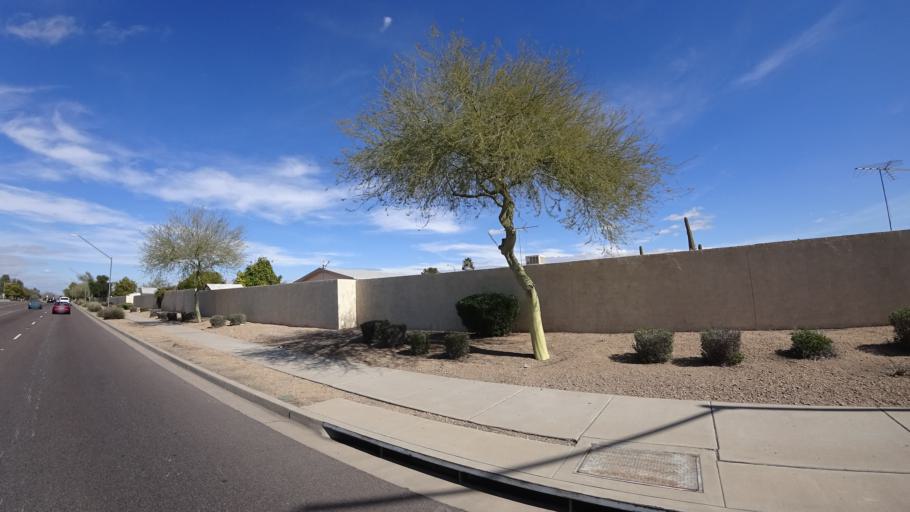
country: US
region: Arizona
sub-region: Maricopa County
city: Peoria
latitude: 33.6418
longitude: -112.2029
